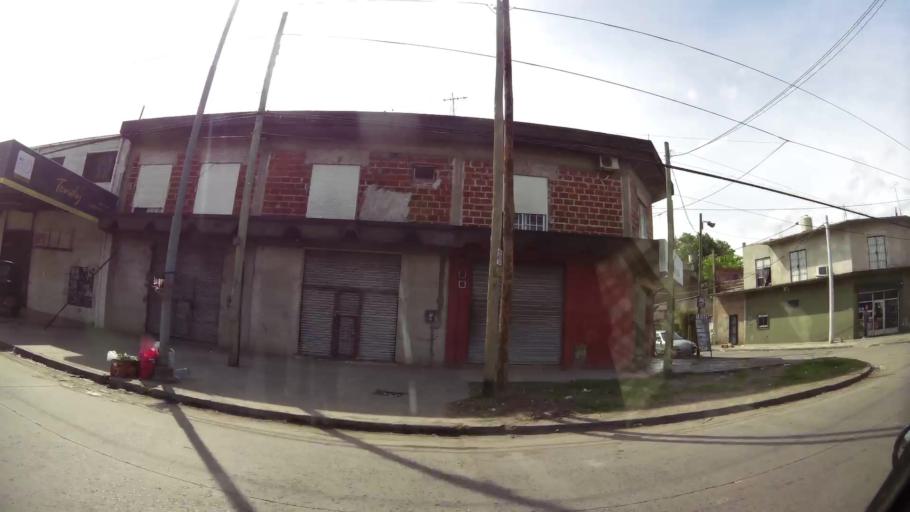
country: AR
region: Buenos Aires
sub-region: Partido de Quilmes
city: Quilmes
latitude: -34.7617
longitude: -58.2447
